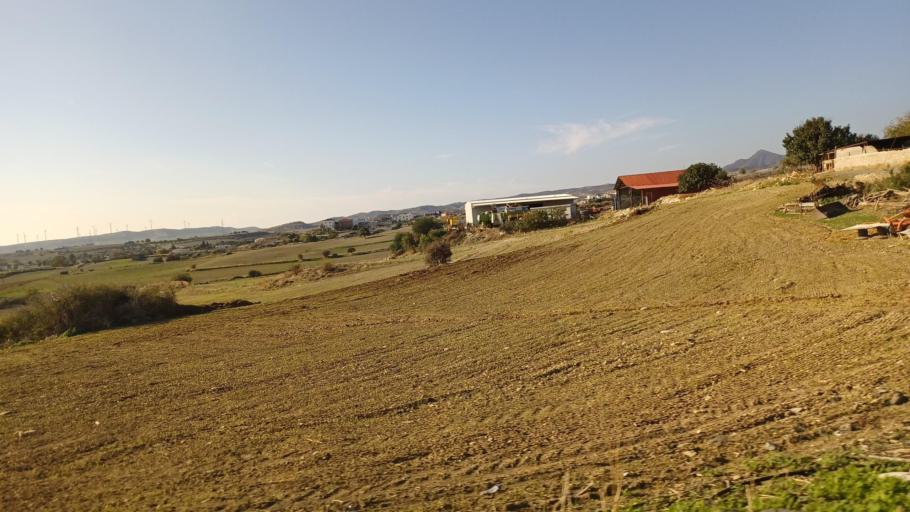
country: CY
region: Larnaka
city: Aradippou
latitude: 34.9363
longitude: 33.5288
